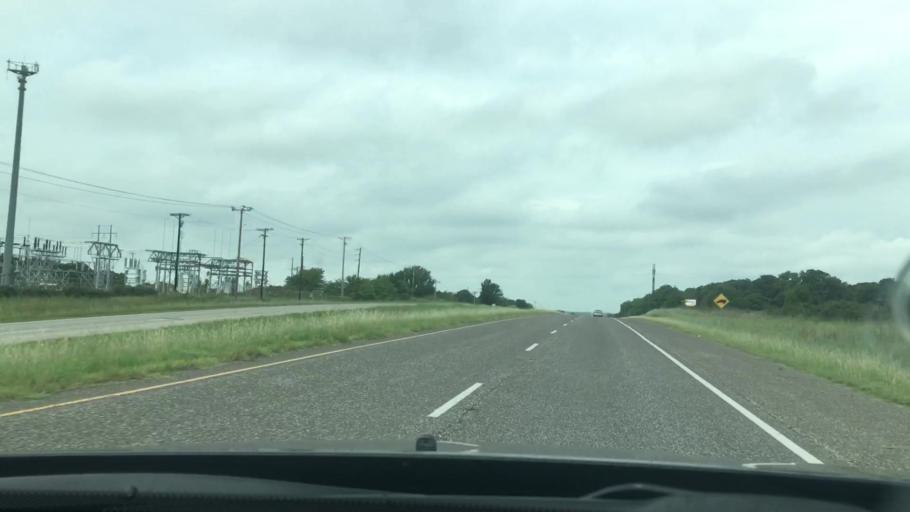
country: US
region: Oklahoma
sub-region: Carter County
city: Lone Grove
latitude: 34.1730
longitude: -97.3307
